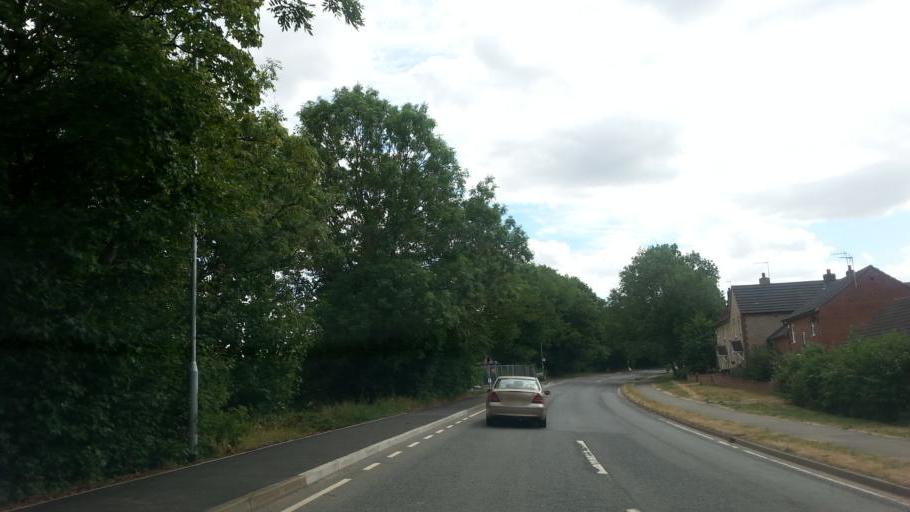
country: GB
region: England
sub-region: Northamptonshire
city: Silverstone
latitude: 52.0900
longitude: -1.0219
